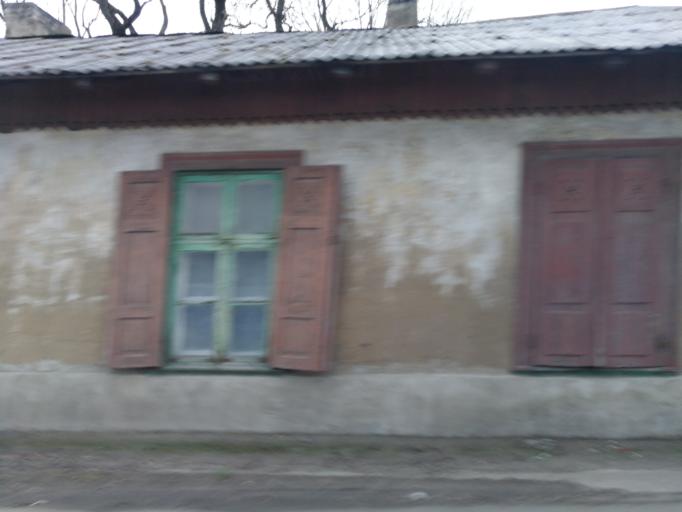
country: LV
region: Marupe
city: Marupe
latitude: 56.9389
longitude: 24.0489
